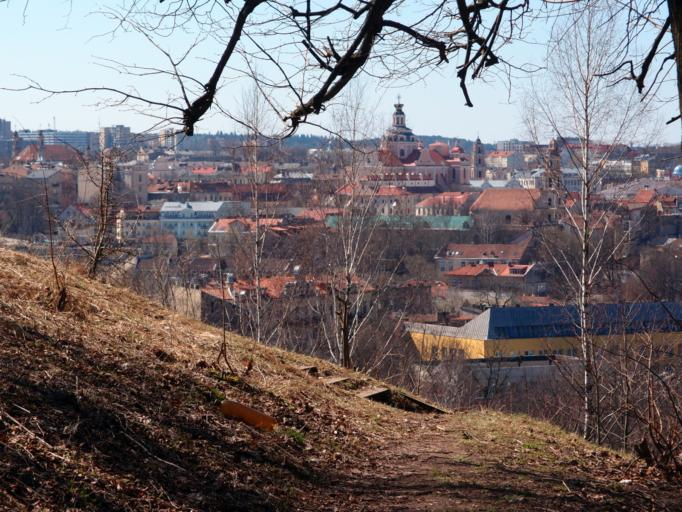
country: LT
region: Vilnius County
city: Rasos
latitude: 54.6842
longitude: 25.3003
